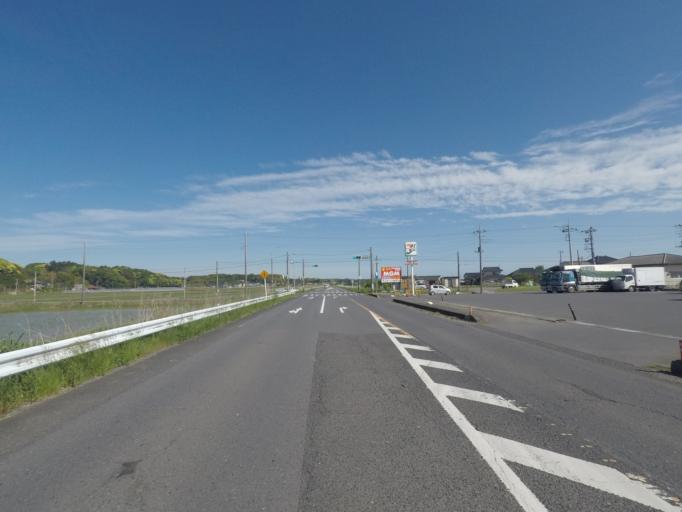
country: JP
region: Ibaraki
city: Inashiki
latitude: 36.0536
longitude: 140.4399
